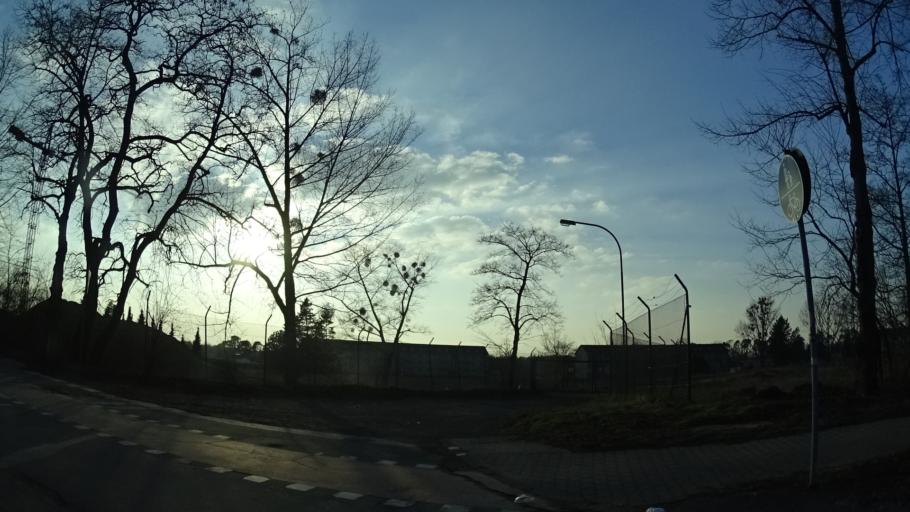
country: DE
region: Hesse
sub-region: Regierungsbezirk Darmstadt
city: Darmstadt
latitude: 49.8482
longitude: 8.6462
